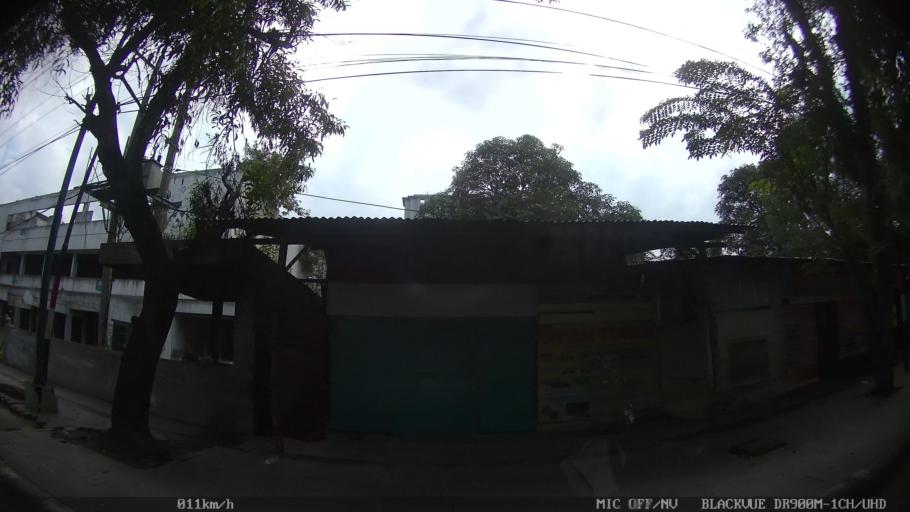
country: ID
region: North Sumatra
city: Medan
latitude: 3.5947
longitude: 98.6790
